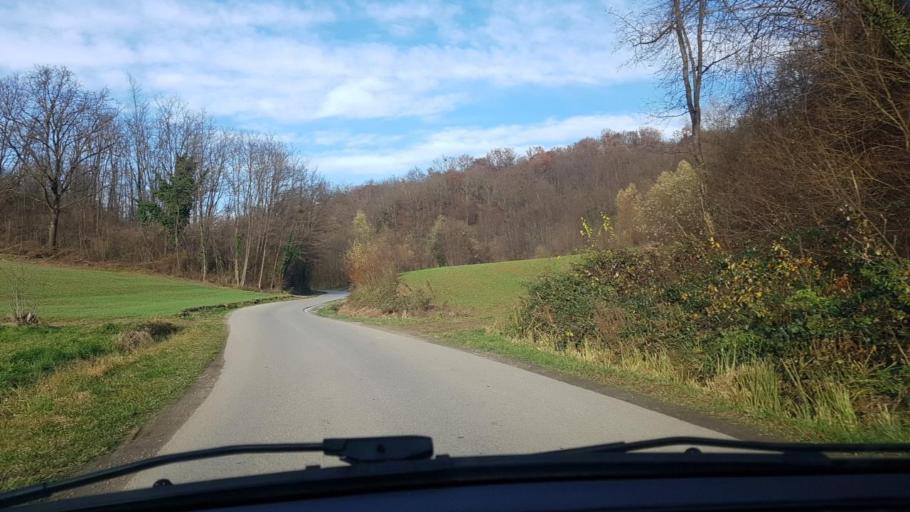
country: HR
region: Krapinsko-Zagorska
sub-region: Grad Krapina
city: Krapina
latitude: 46.1281
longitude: 15.8717
